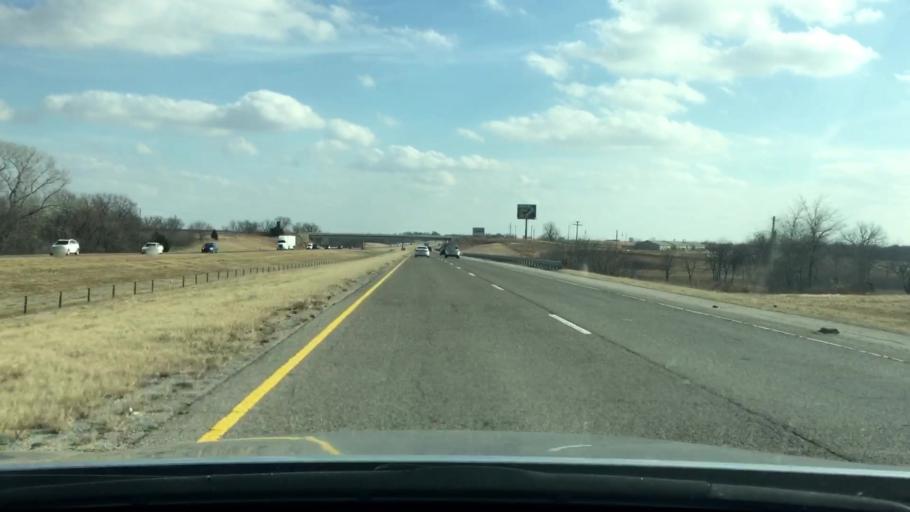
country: US
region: Oklahoma
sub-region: Garvin County
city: Maysville
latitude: 34.8994
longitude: -97.3474
